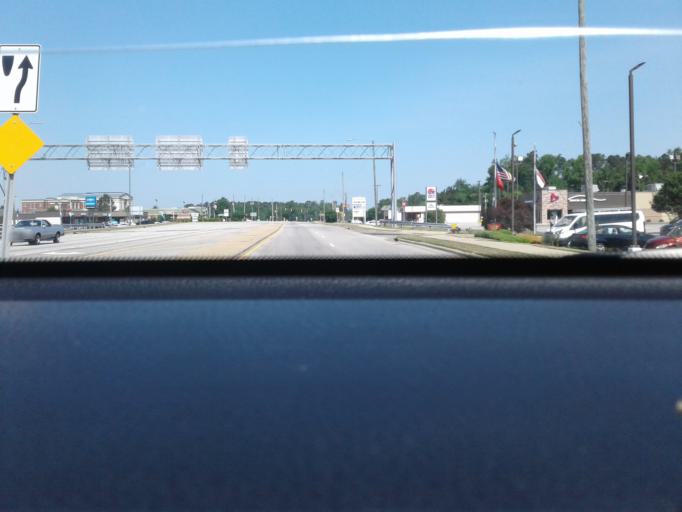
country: US
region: North Carolina
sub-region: Harnett County
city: Lillington
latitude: 35.4182
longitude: -78.8037
